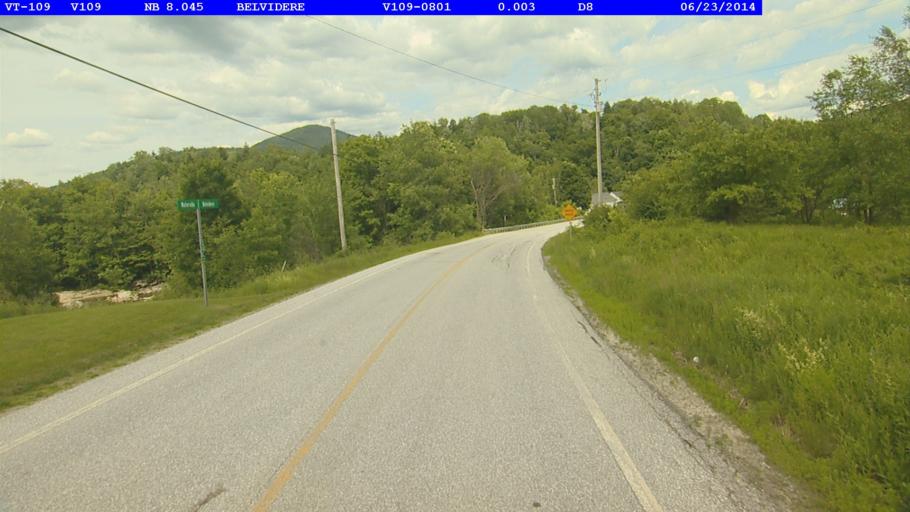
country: US
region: Vermont
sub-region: Lamoille County
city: Johnson
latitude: 44.7371
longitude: -72.7435
